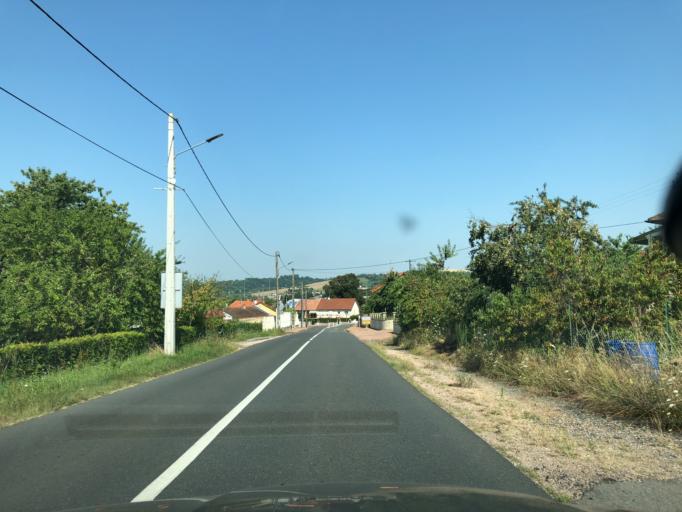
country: FR
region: Auvergne
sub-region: Departement de l'Allier
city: Cusset
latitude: 46.1315
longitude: 3.4750
